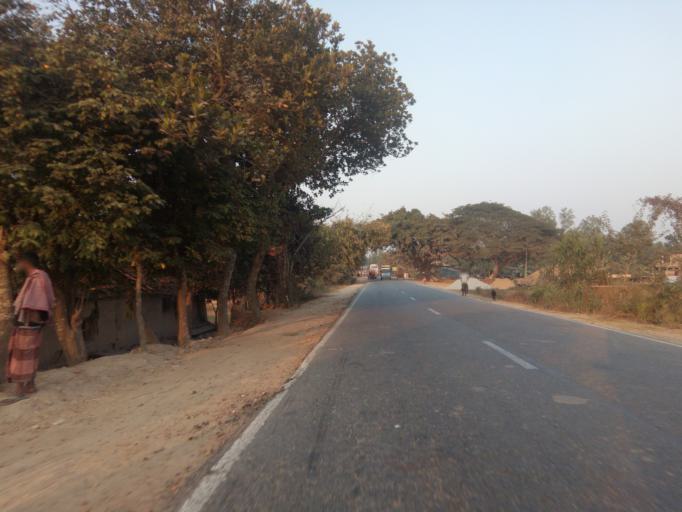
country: BD
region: Rajshahi
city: Bogra
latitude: 24.5908
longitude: 89.2349
